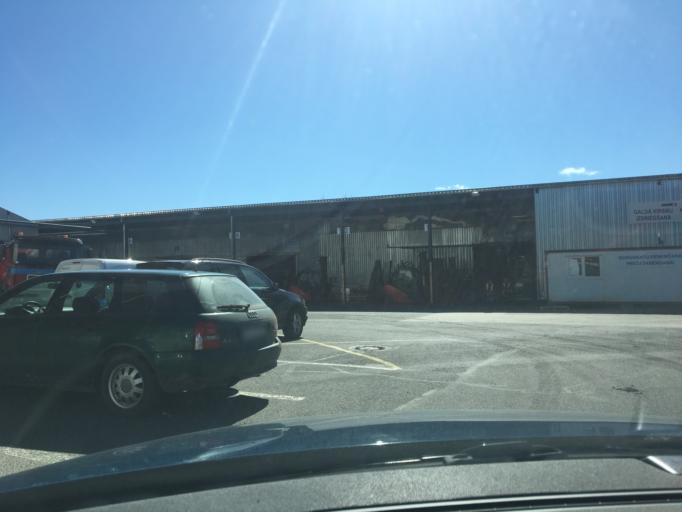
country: LV
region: Kekava
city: Kekava
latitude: 56.8799
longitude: 24.2450
